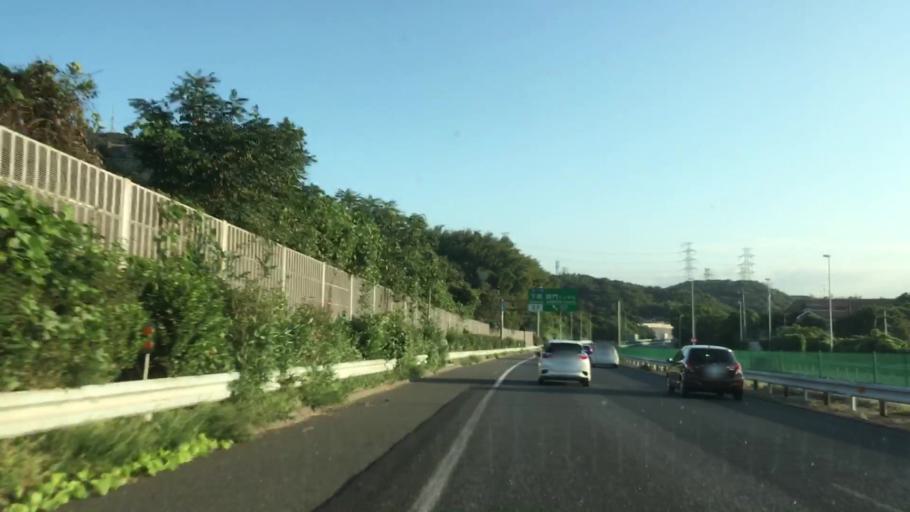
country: JP
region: Yamaguchi
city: Shimonoseki
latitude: 33.9818
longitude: 130.9524
